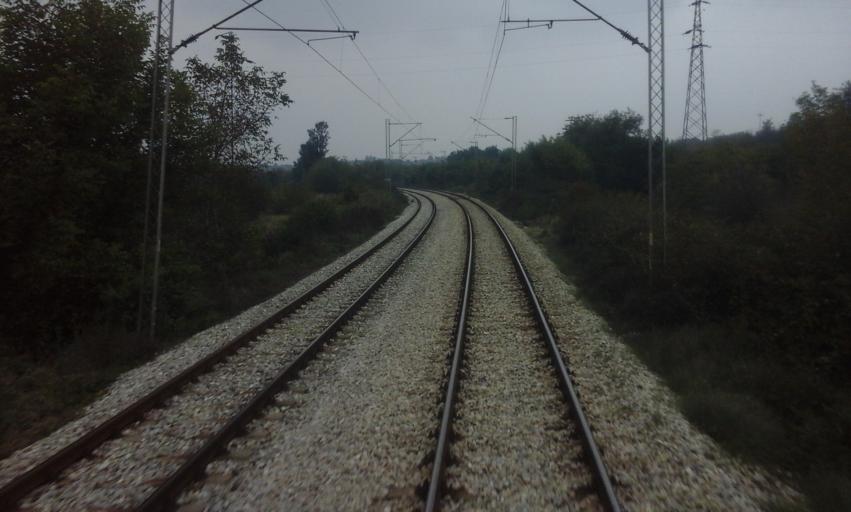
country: RS
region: Central Serbia
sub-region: Sumadijski Okrug
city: Lapovo
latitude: 44.2095
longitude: 21.0930
